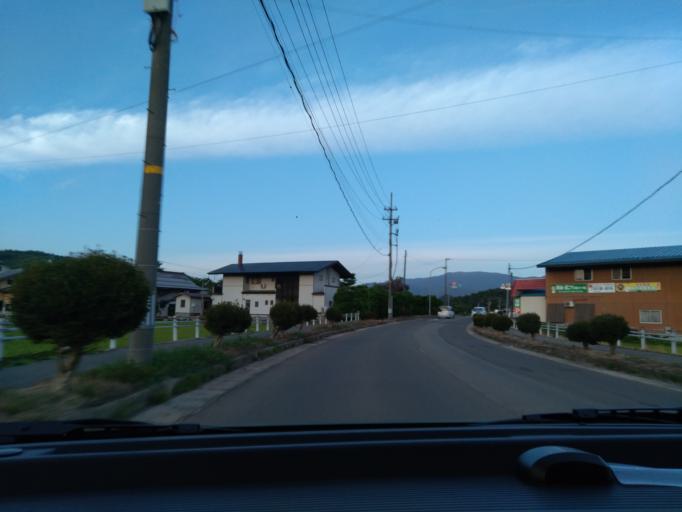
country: JP
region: Akita
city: Kakunodatemachi
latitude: 39.5919
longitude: 140.5562
